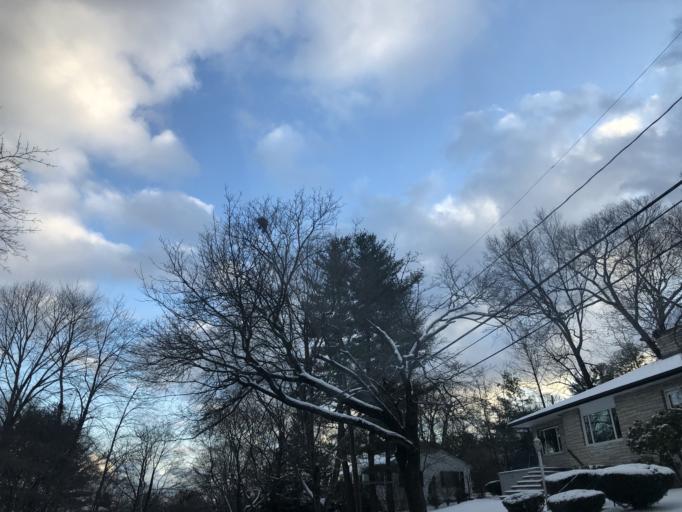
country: US
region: Massachusetts
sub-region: Middlesex County
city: Arlington
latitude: 42.4265
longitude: -71.1583
